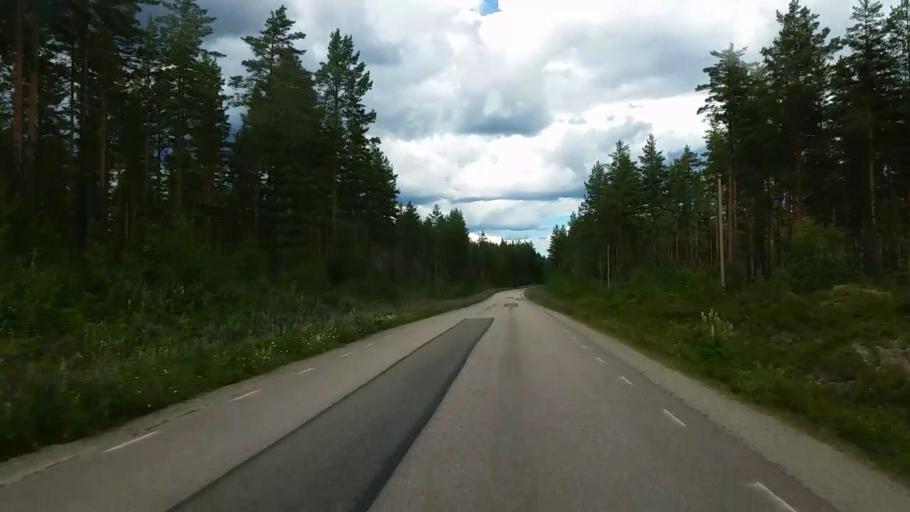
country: SE
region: Gaevleborg
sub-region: Ovanakers Kommun
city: Edsbyn
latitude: 61.4073
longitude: 15.8967
